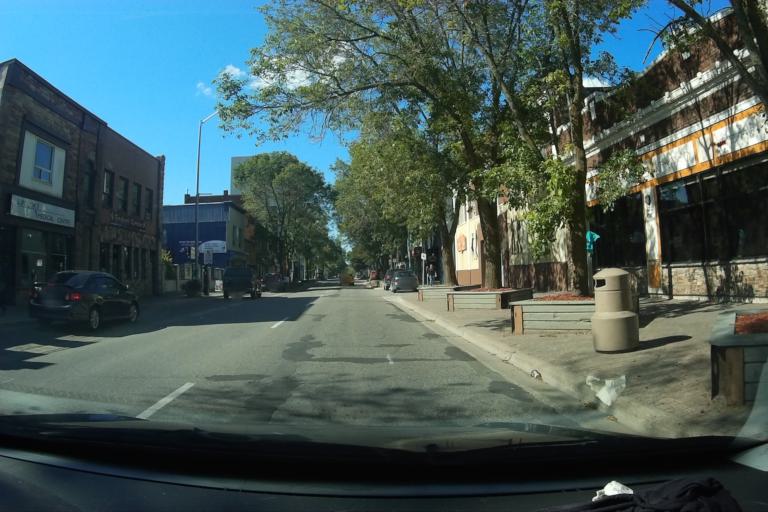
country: CA
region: Ontario
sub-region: Algoma
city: Sault Ste. Marie
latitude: 46.5080
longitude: -84.3283
